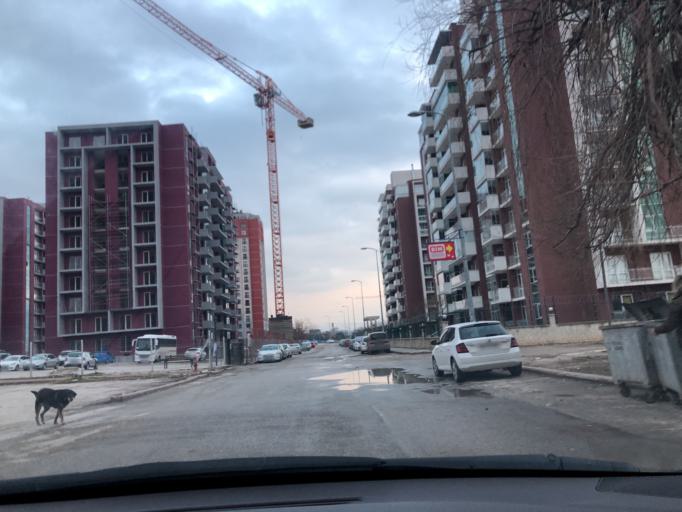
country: TR
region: Ankara
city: Batikent
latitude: 39.9641
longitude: 32.7736
